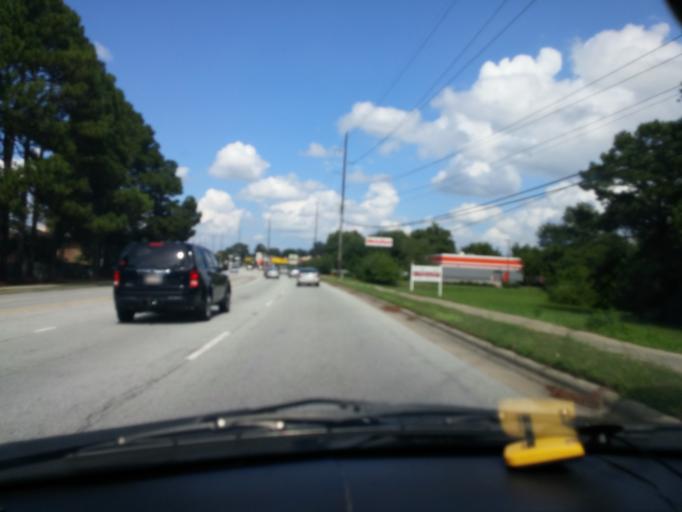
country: US
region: North Carolina
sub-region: Pitt County
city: Greenville
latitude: 35.5941
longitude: -77.3399
